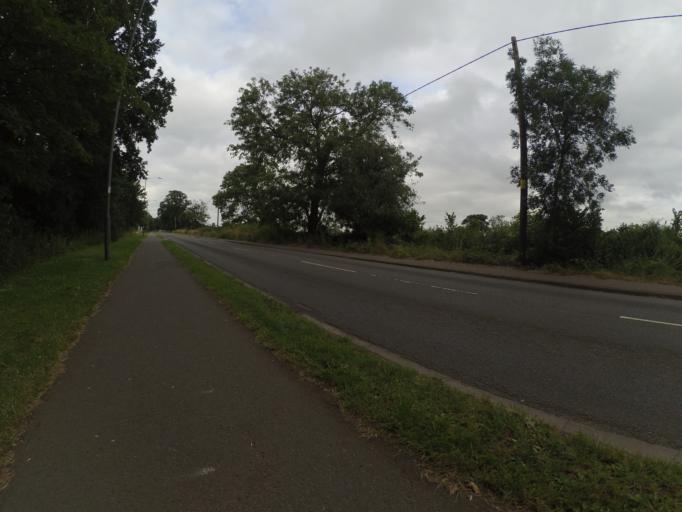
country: GB
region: England
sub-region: Warwickshire
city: Rugby
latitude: 52.3514
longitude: -1.2513
